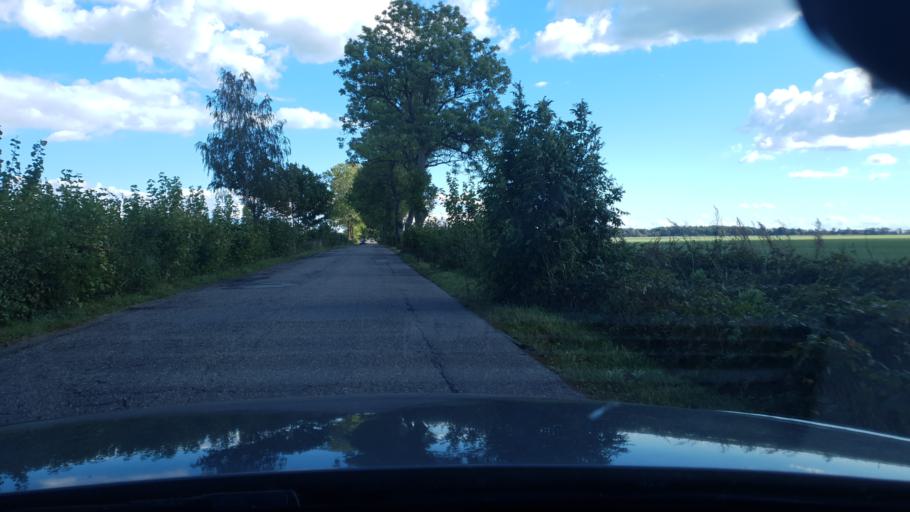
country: PL
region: Pomeranian Voivodeship
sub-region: Powiat pucki
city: Zelistrzewo
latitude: 54.6879
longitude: 18.4349
